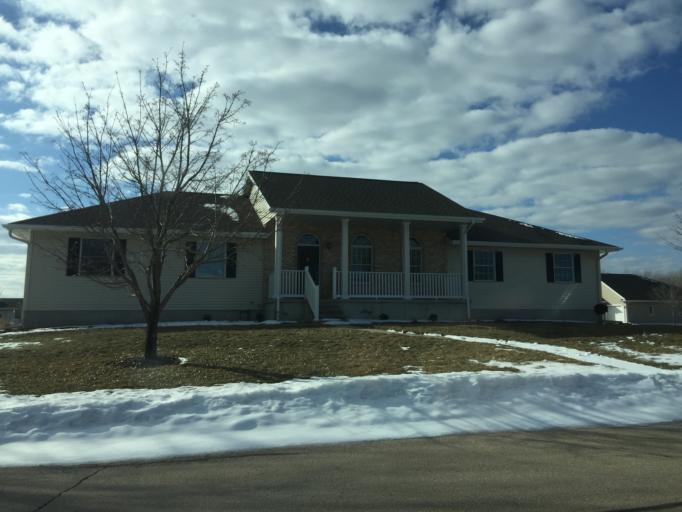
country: US
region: Michigan
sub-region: Menominee County
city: Menominee
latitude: 45.1221
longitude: -87.6255
